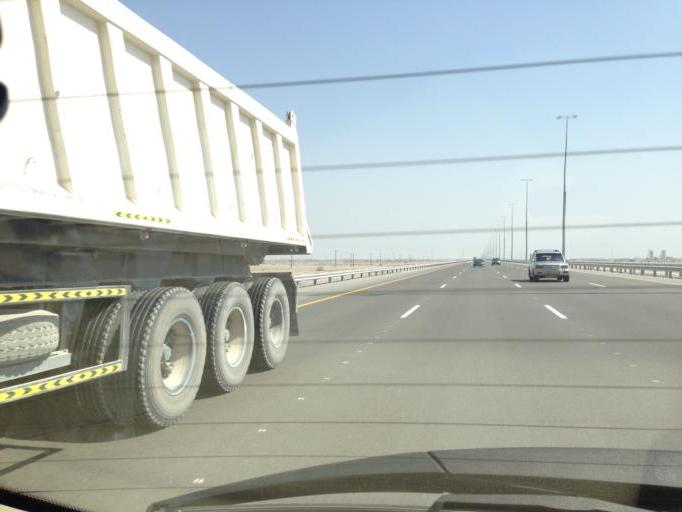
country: OM
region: Al Batinah
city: Barka'
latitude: 23.5922
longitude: 57.8072
